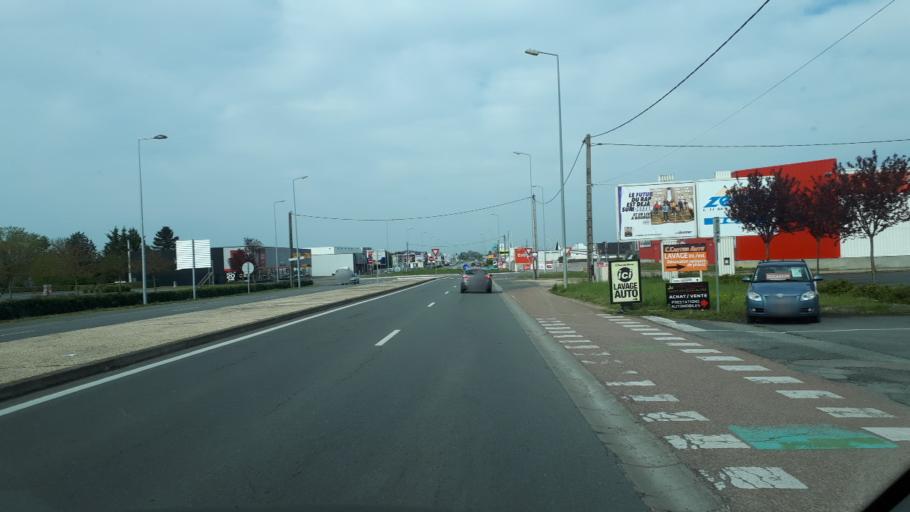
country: FR
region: Centre
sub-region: Departement du Cher
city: Saint-Germain-du-Puy
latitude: 47.0971
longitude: 2.4537
